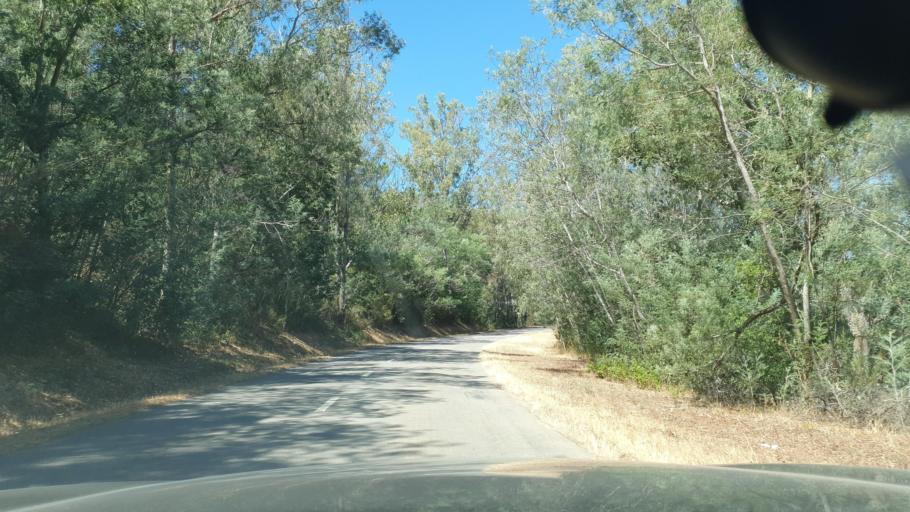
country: PT
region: Beja
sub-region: Odemira
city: Odemira
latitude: 37.5084
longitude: -8.4700
